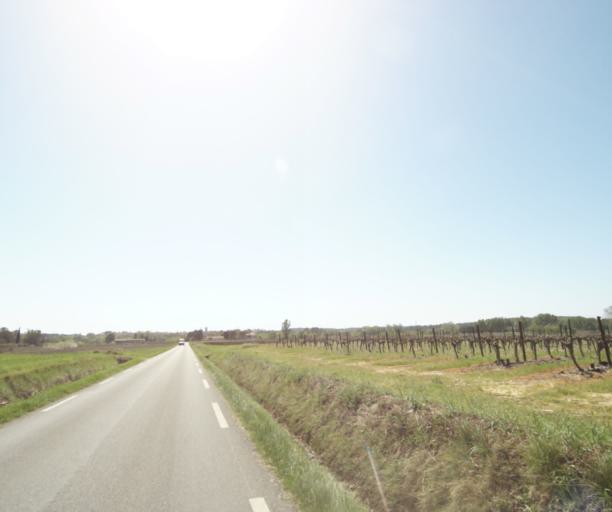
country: FR
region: Languedoc-Roussillon
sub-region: Departement de l'Herault
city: Beaulieu
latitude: 43.7256
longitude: 4.0085
